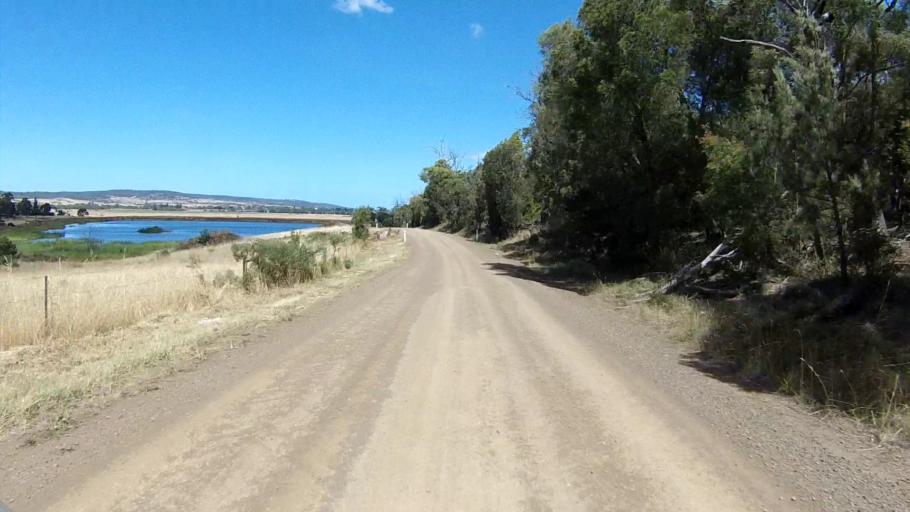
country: AU
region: Tasmania
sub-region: Break O'Day
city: St Helens
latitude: -41.9841
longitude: 148.0655
